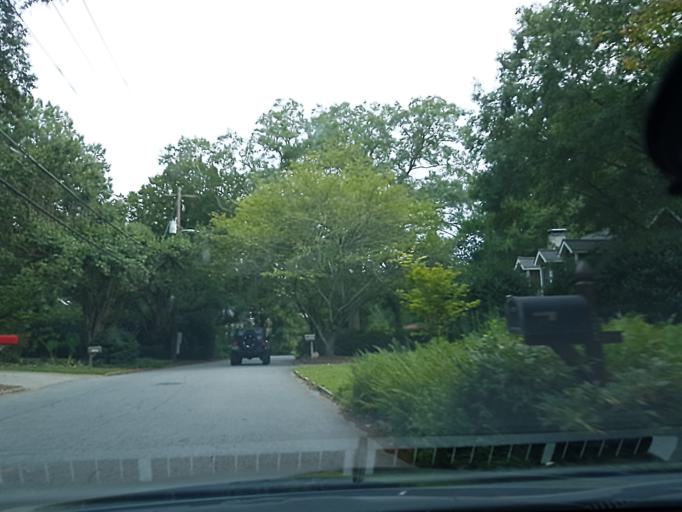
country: US
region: Georgia
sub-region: DeKalb County
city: Druid Hills
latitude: 33.7865
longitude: -84.3456
